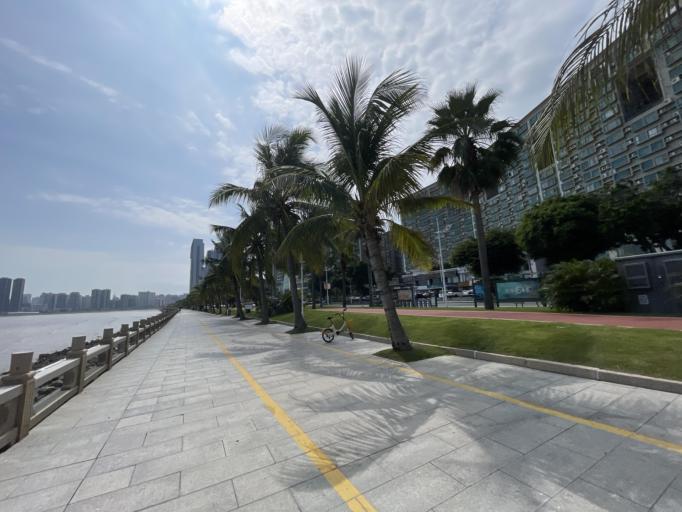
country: CN
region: Guangdong
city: Jida
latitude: 22.2291
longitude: 113.5588
